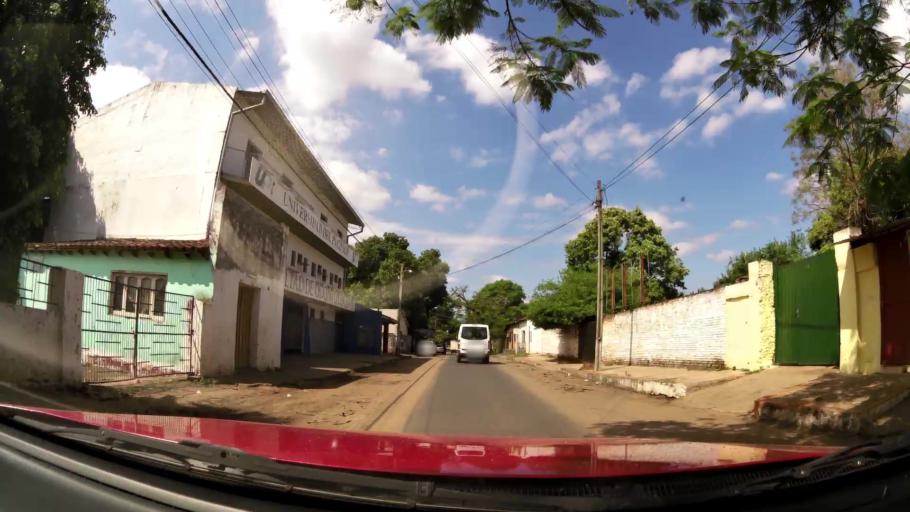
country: PY
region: Central
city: San Lorenzo
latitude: -25.3394
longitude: -57.5077
